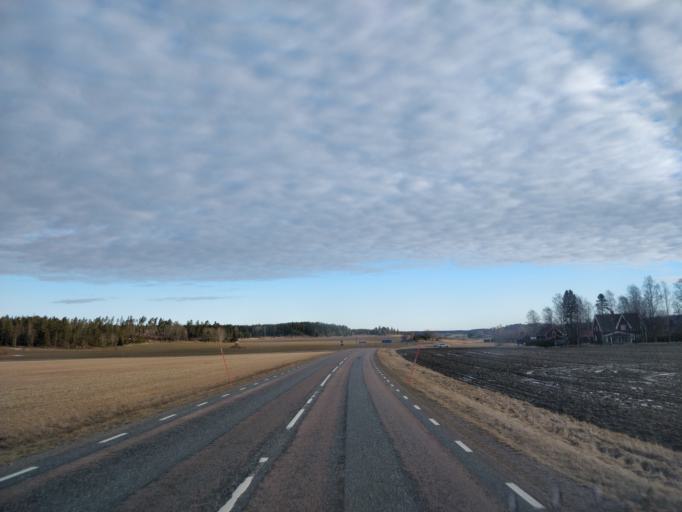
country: SE
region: Uppsala
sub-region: Enkopings Kommun
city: Enkoping
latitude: 59.7656
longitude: 17.0805
